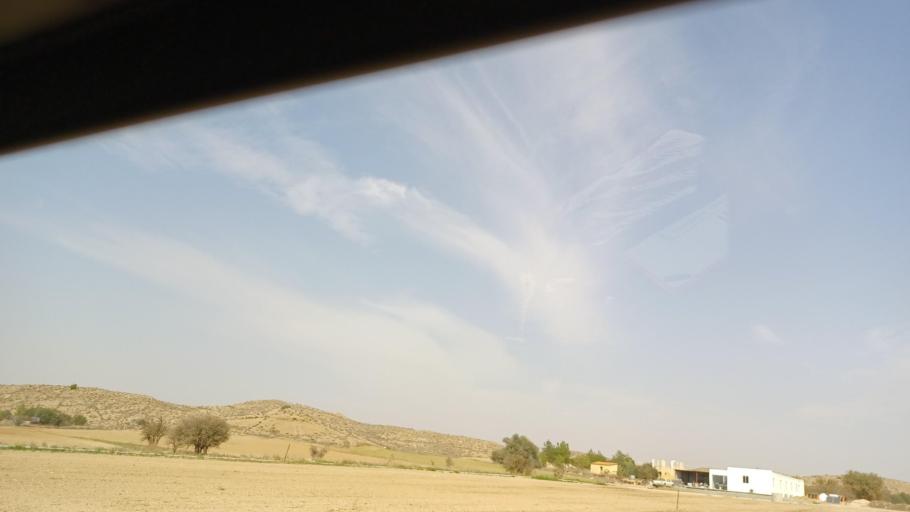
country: CY
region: Larnaka
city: Psevdas
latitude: 34.9710
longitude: 33.4492
